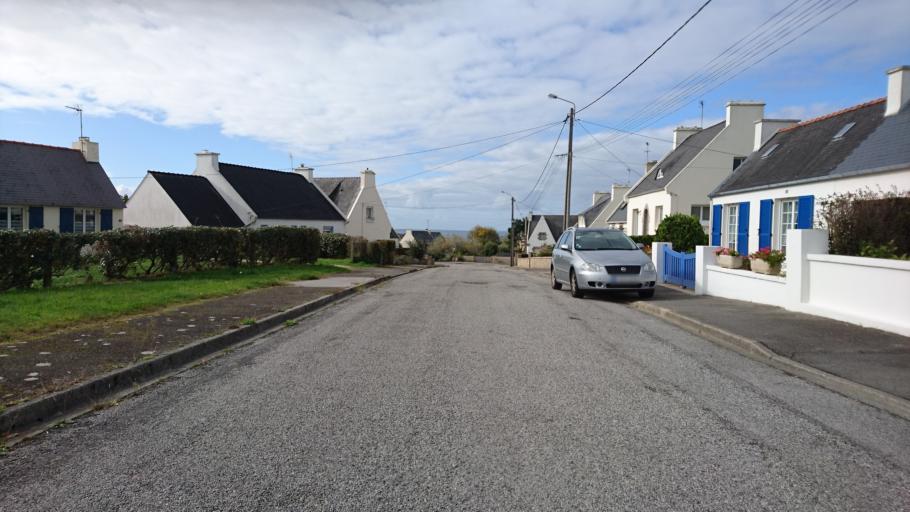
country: FR
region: Brittany
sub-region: Departement du Finistere
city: Lampaul-Plouarzel
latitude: 48.4467
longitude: -4.7702
